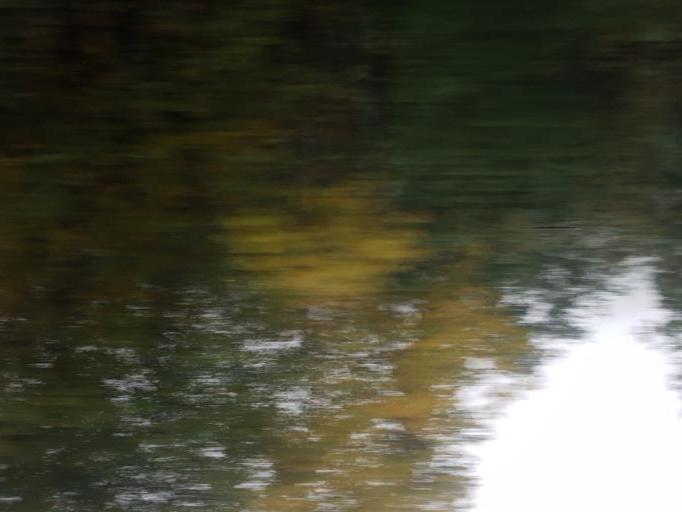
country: NO
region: Sor-Trondelag
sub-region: Trondheim
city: Trondheim
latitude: 63.3698
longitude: 10.3628
